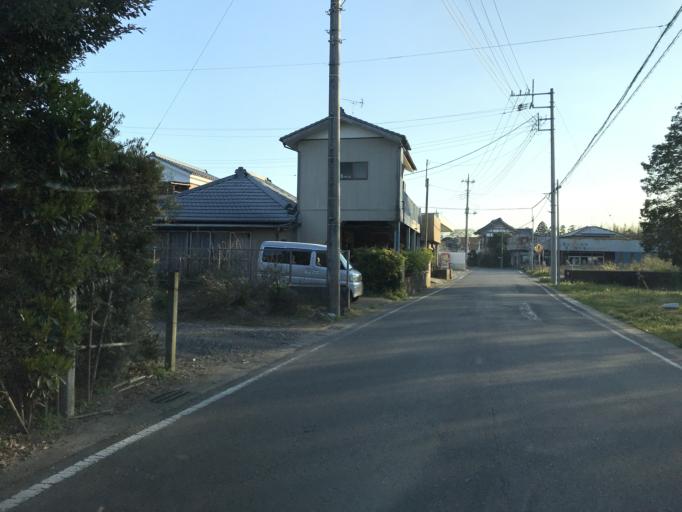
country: JP
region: Chiba
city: Yokaichiba
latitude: 35.7577
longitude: 140.5777
